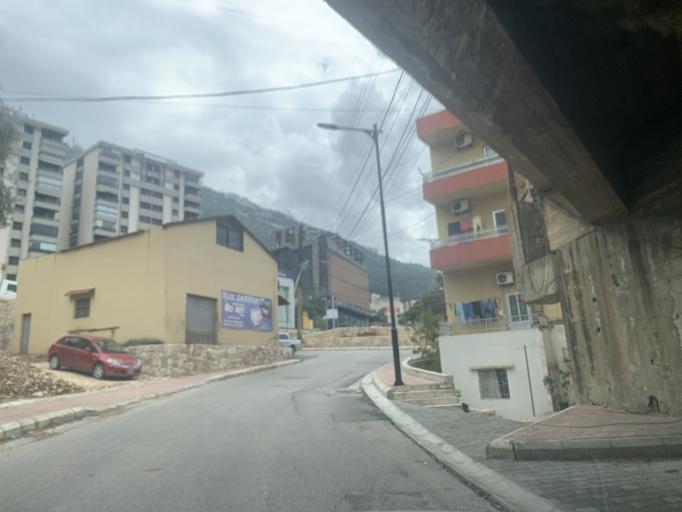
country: LB
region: Mont-Liban
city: Djounie
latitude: 33.9894
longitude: 35.6439
